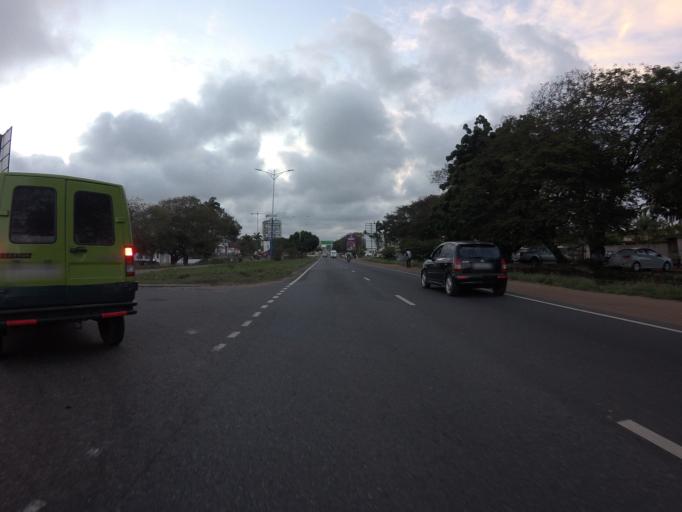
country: GH
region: Greater Accra
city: Accra
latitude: 5.5644
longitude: -0.1762
